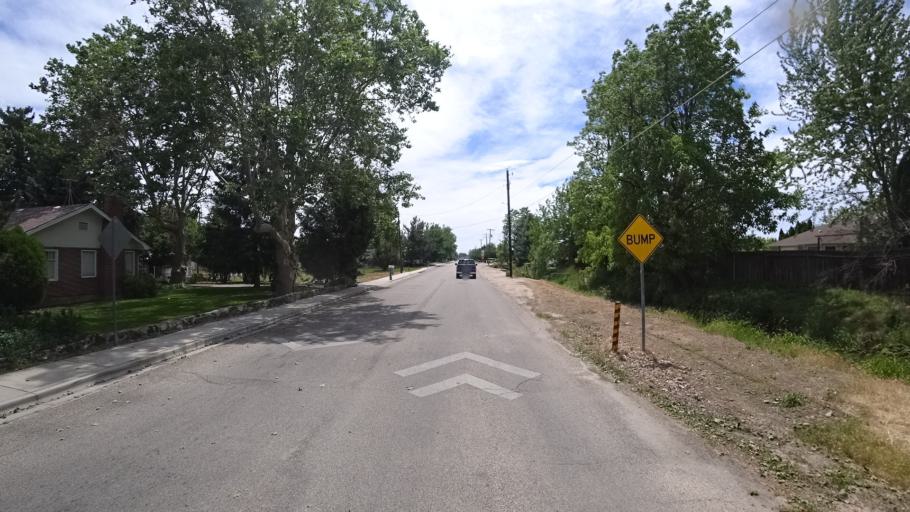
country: US
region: Idaho
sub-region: Ada County
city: Meridian
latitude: 43.6245
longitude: -116.3202
